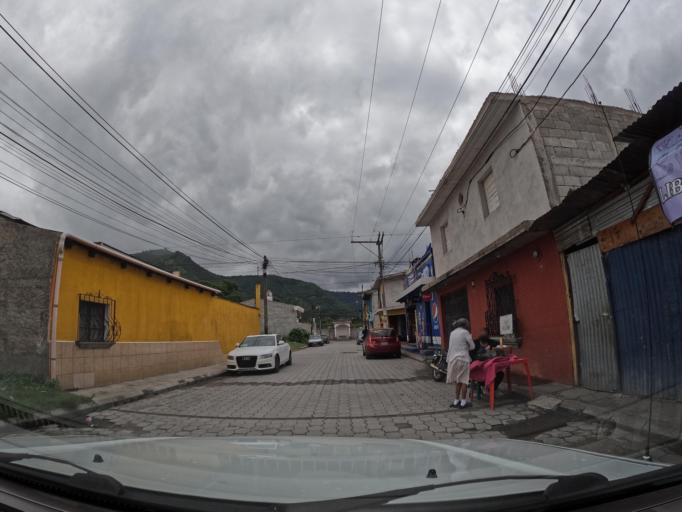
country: GT
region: Sacatepequez
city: Jocotenango
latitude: 14.5801
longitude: -90.7468
